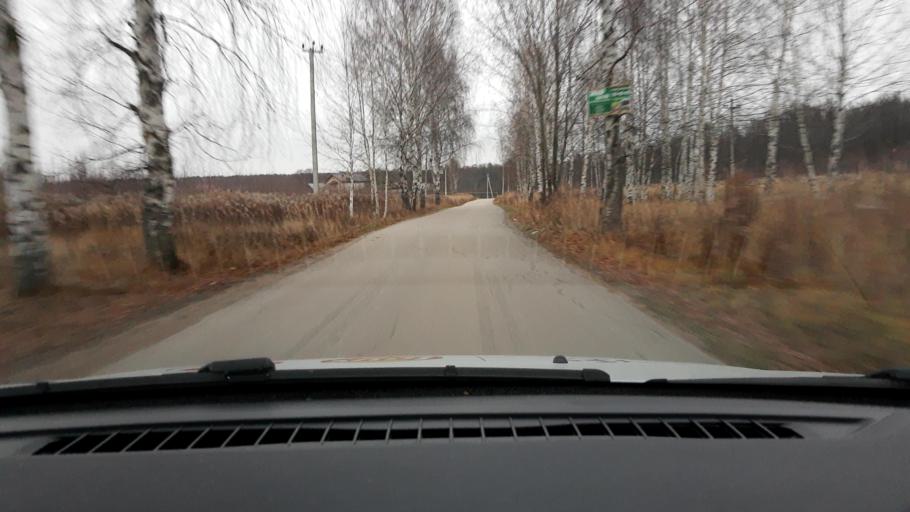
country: RU
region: Nizjnij Novgorod
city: Neklyudovo
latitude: 56.4153
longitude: 44.0152
